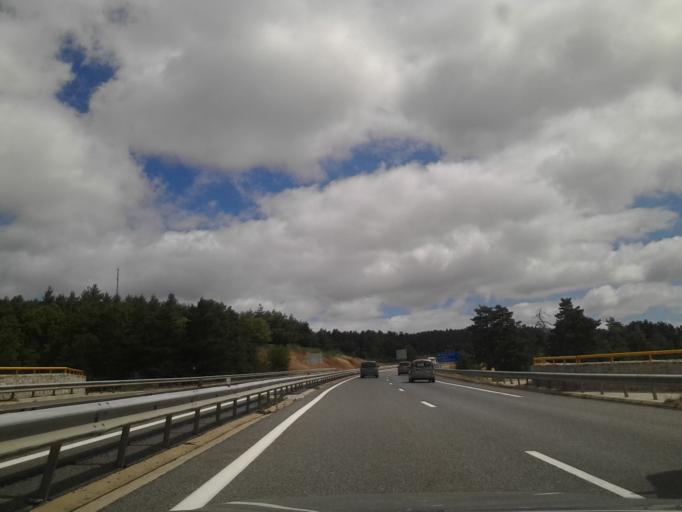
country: FR
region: Midi-Pyrenees
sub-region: Departement de l'Aveyron
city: Severac-le-Chateau
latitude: 44.3928
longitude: 3.1247
